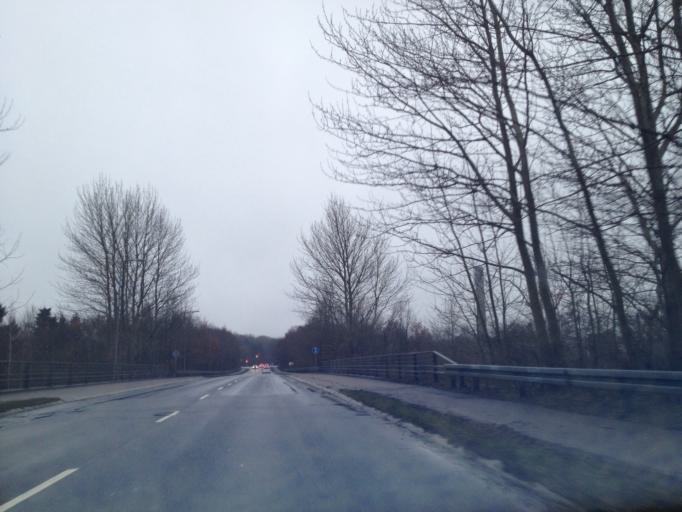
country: DK
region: Capital Region
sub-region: Hoje-Taastrup Kommune
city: Flong
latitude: 55.6507
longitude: 12.1775
